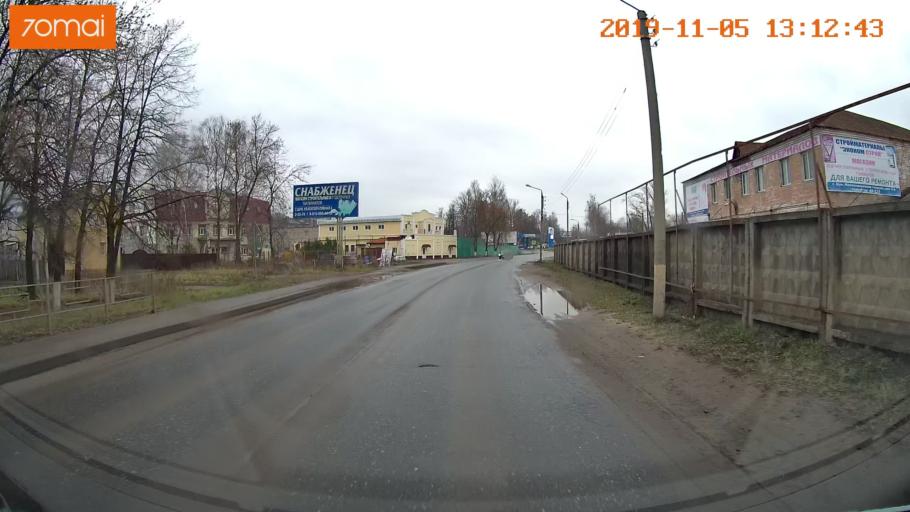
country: RU
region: Ivanovo
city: Shuya
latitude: 56.8559
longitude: 41.3530
